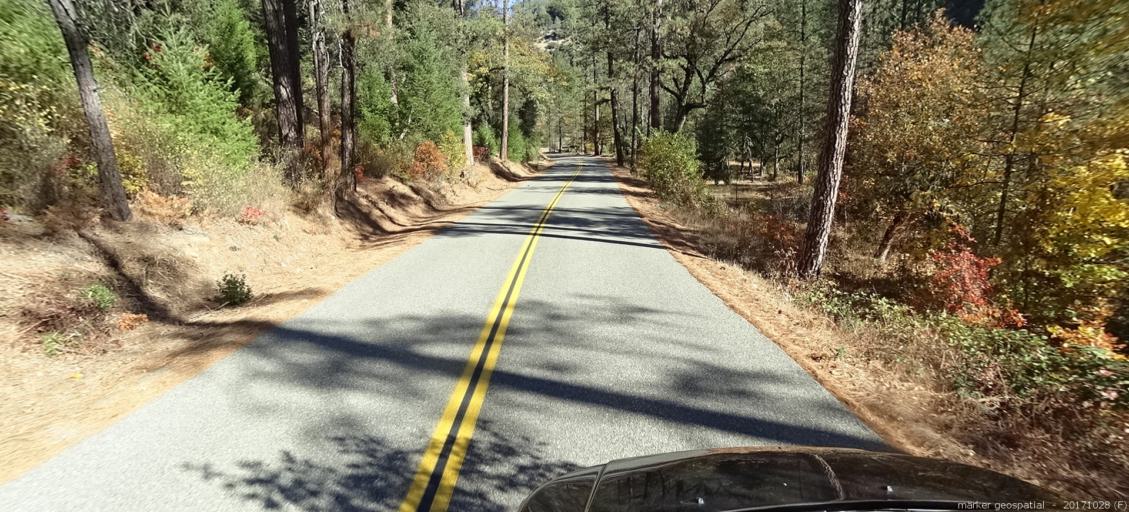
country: US
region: California
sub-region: Trinity County
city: Lewiston
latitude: 40.7861
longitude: -122.6102
